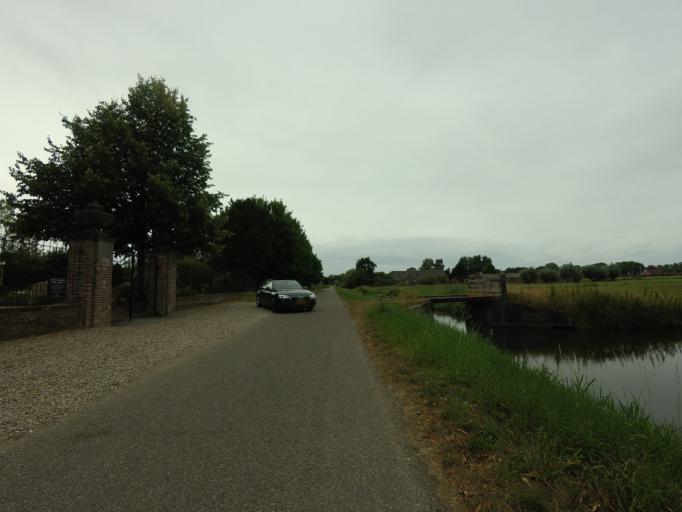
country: NL
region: Utrecht
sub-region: Stichtse Vecht
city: Maarssen
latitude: 52.1327
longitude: 5.0686
